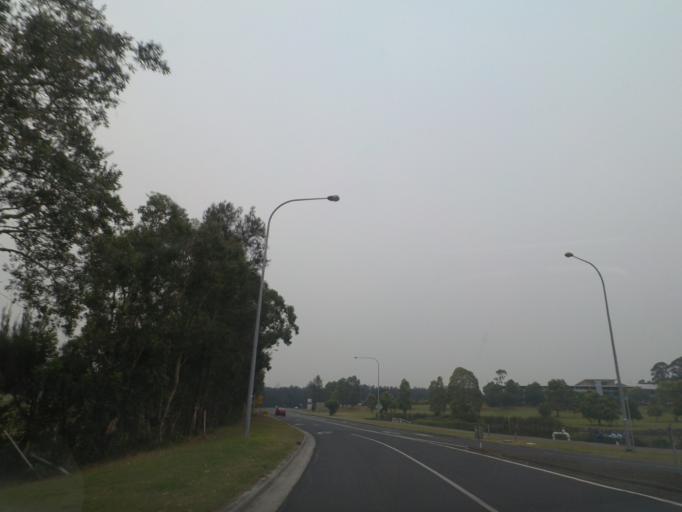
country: AU
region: New South Wales
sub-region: Coffs Harbour
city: Toormina
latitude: -30.3257
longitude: 153.0987
